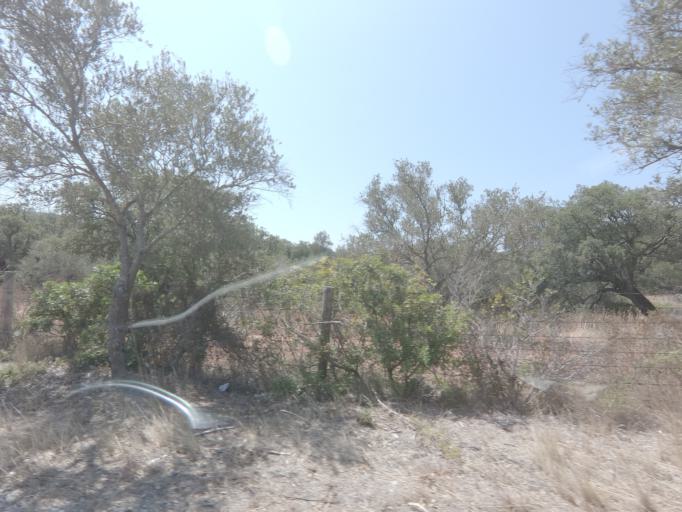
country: PT
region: Setubal
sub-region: Setubal
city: Setubal
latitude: 38.5223
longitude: -8.9318
